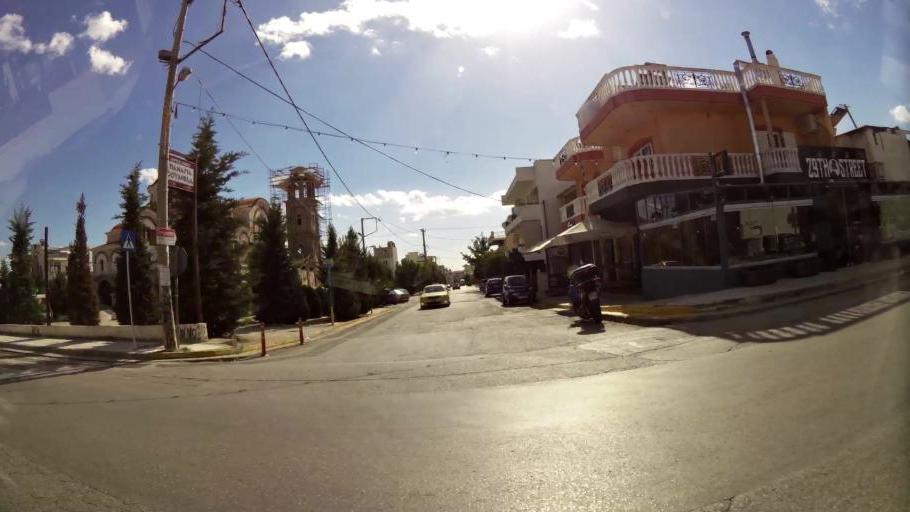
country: GR
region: Attica
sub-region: Nomarchia Anatolikis Attikis
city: Acharnes
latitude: 38.0978
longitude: 23.7282
